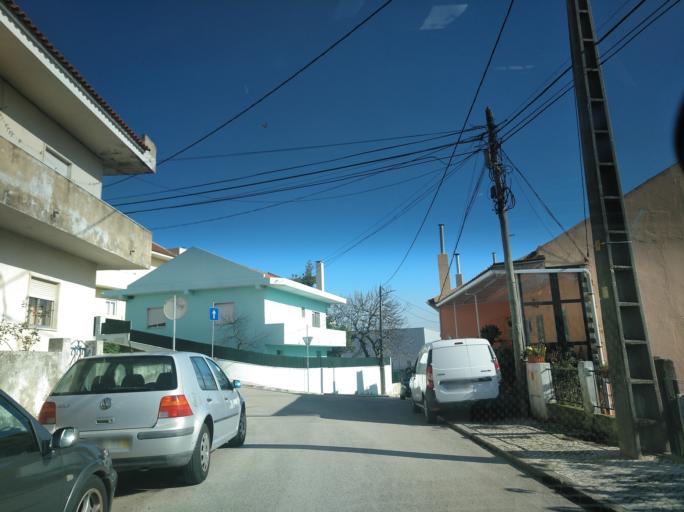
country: PT
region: Lisbon
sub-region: Odivelas
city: Famoes
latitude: 38.7914
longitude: -9.2196
